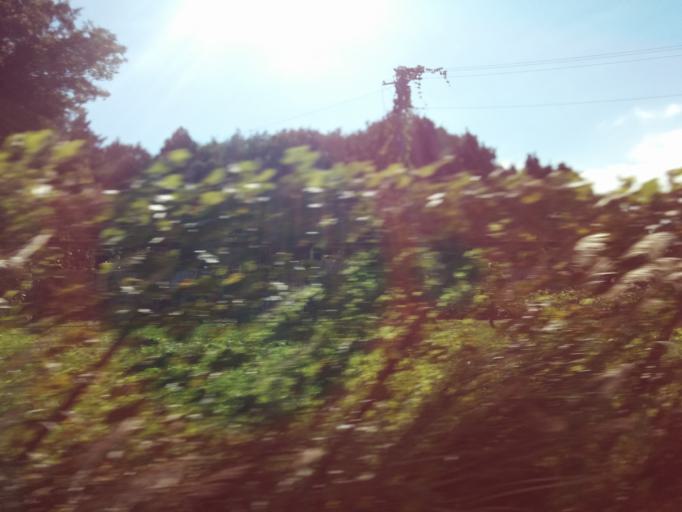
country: JP
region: Kanagawa
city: Minami-rinkan
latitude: 35.4179
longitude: 139.4339
